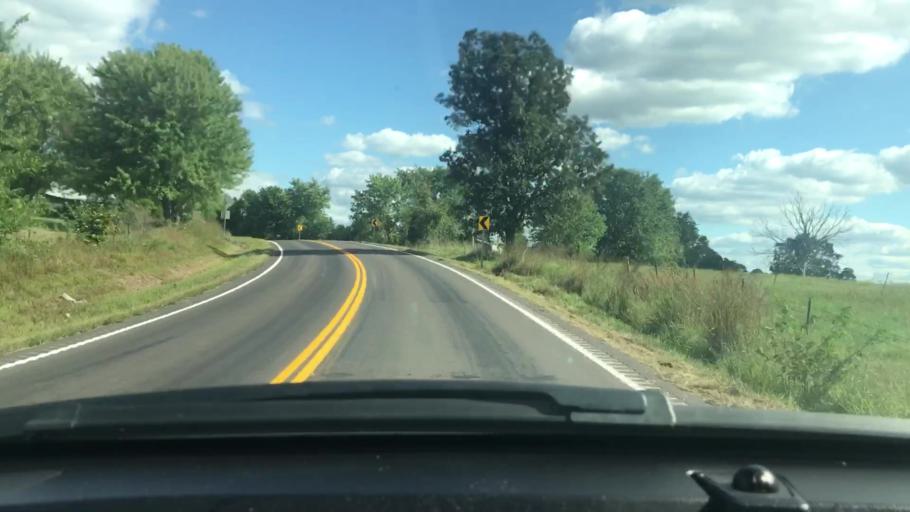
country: US
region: Missouri
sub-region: Wright County
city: Mountain Grove
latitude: 37.2554
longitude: -92.3075
